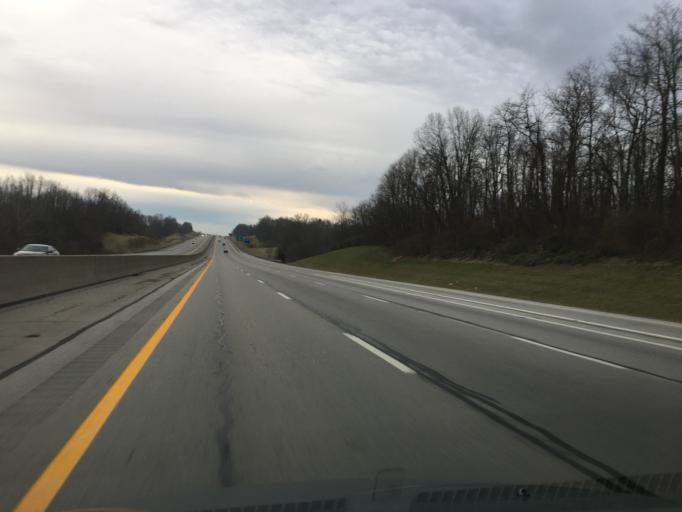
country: US
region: Kentucky
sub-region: Grant County
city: Crittenden
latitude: 38.8124
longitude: -84.6017
